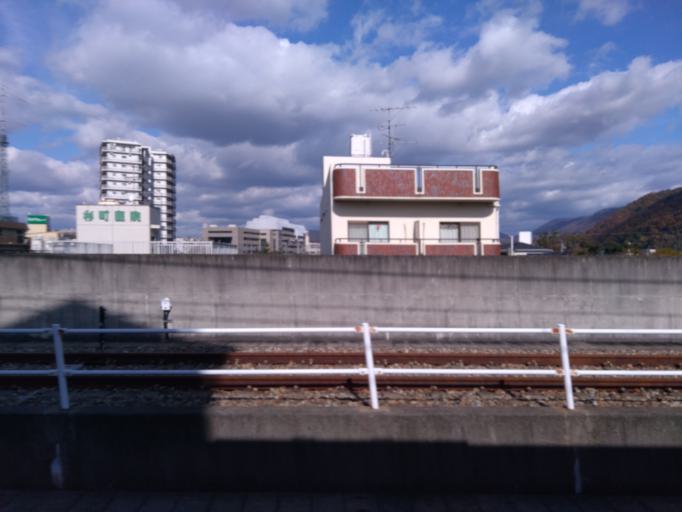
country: JP
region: Hyogo
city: Kawanishi
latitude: 34.8269
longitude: 135.4166
